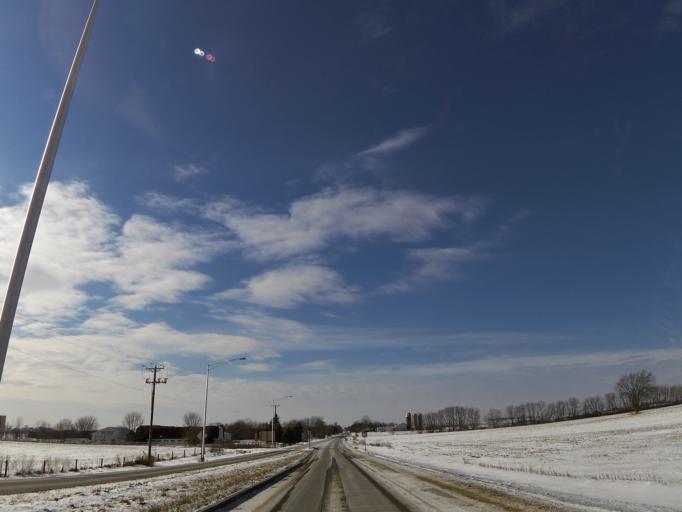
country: US
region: Wisconsin
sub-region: Saint Croix County
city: Roberts
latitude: 44.9927
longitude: -92.5591
